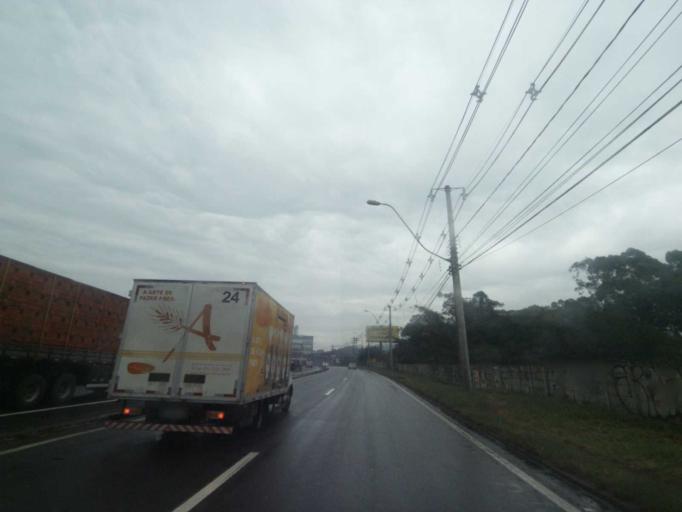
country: BR
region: Rio Grande do Sul
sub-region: Sao Leopoldo
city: Sao Leopoldo
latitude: -29.7837
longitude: -51.1619
